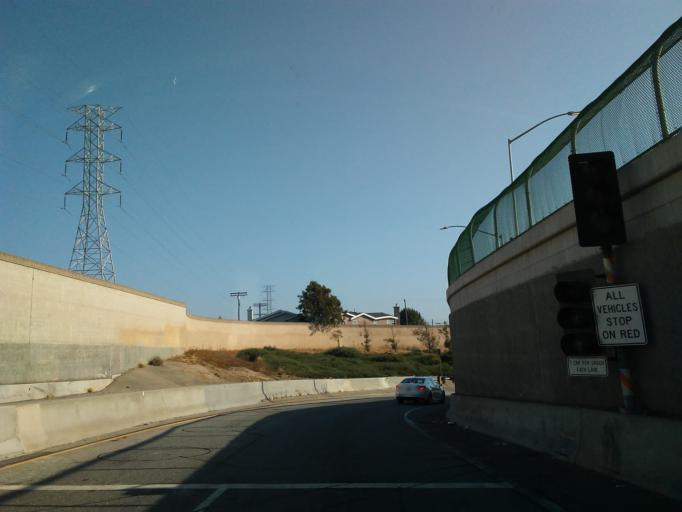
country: US
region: California
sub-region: Los Angeles County
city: West Rancho Dominguez
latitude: 33.9009
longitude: -118.2853
